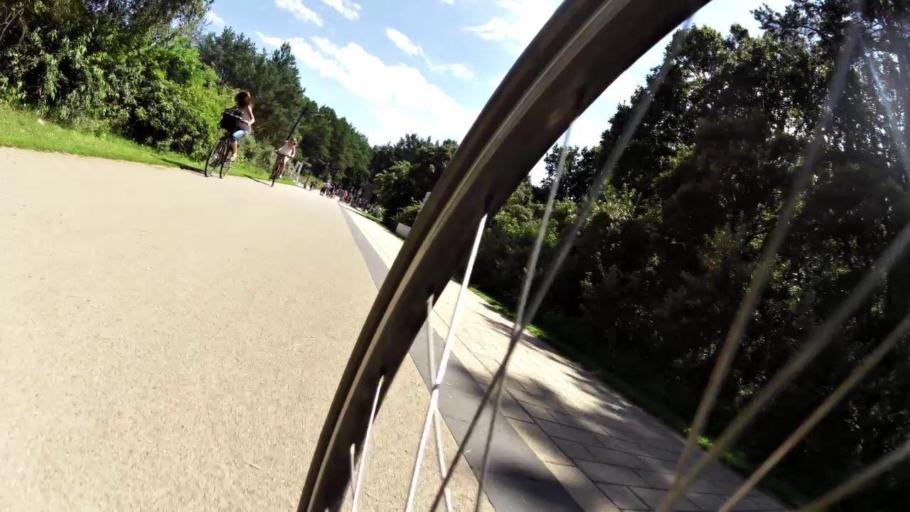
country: PL
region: West Pomeranian Voivodeship
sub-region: Swinoujscie
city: Swinoujscie
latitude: 53.9273
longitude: 14.2240
